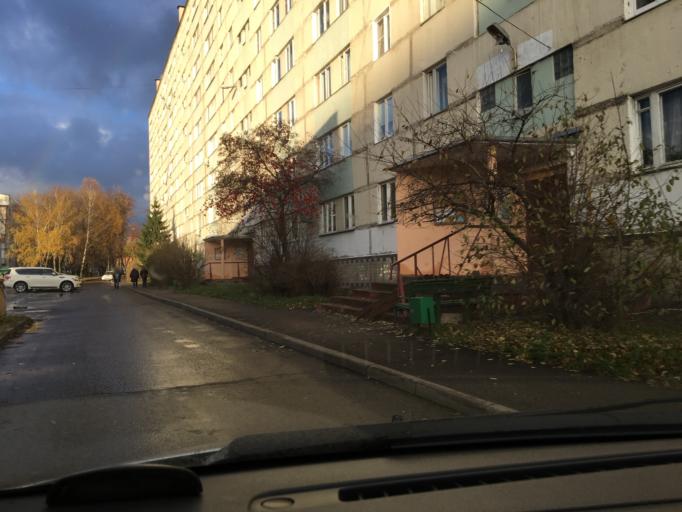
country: RU
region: Moskovskaya
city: Vidnoye
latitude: 55.5499
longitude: 37.7047
